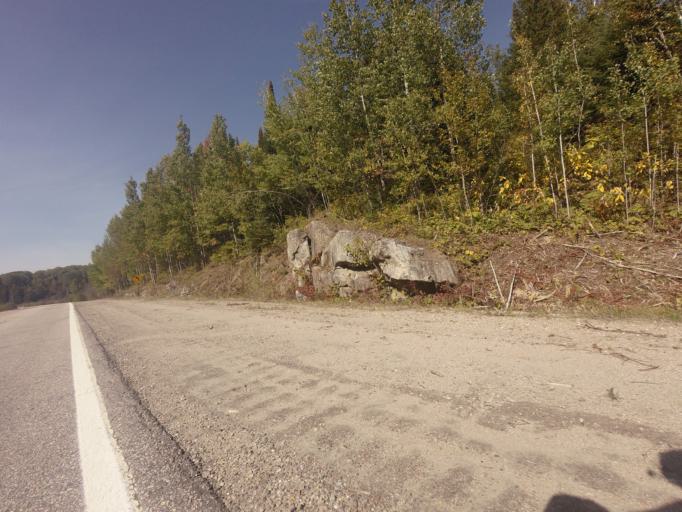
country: CA
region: Quebec
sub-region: Outaouais
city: Maniwaki
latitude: 46.5543
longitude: -75.8081
